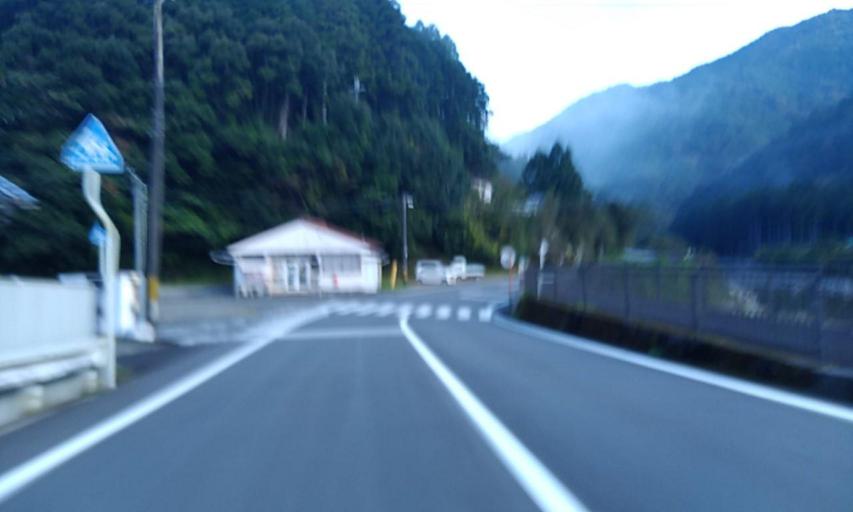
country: JP
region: Wakayama
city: Shingu
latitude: 33.7297
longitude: 135.9100
